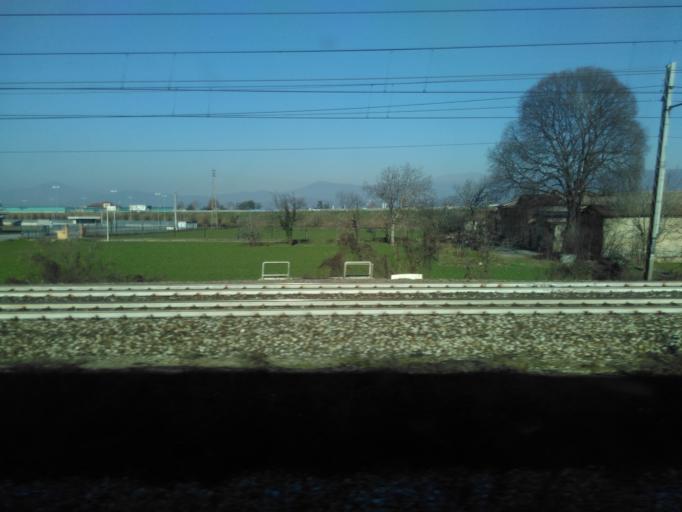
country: IT
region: Lombardy
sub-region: Provincia di Brescia
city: Castegnato
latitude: 45.5480
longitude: 10.1129
